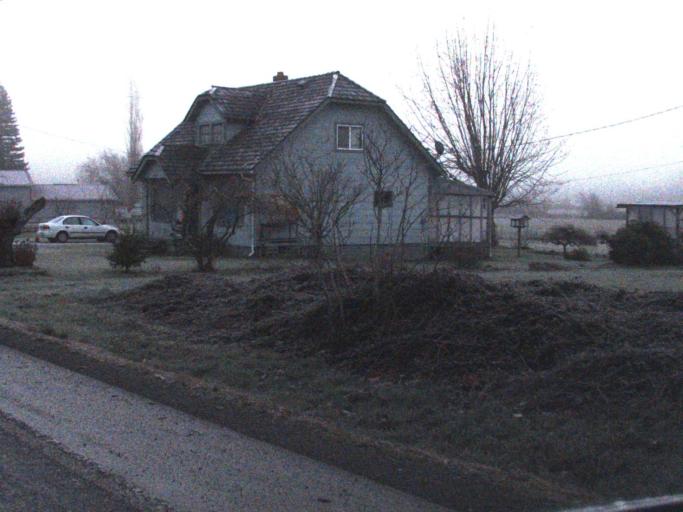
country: US
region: Washington
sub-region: Skagit County
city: Sedro-Woolley
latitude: 48.5246
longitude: -121.9457
